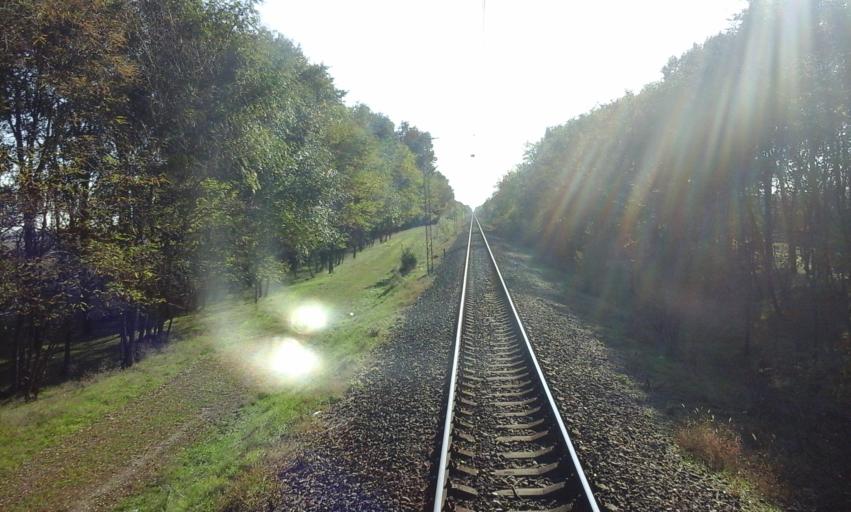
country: RS
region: Autonomna Pokrajina Vojvodina
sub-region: Severnobacki Okrug
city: Backa Topola
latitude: 45.8651
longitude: 19.6568
